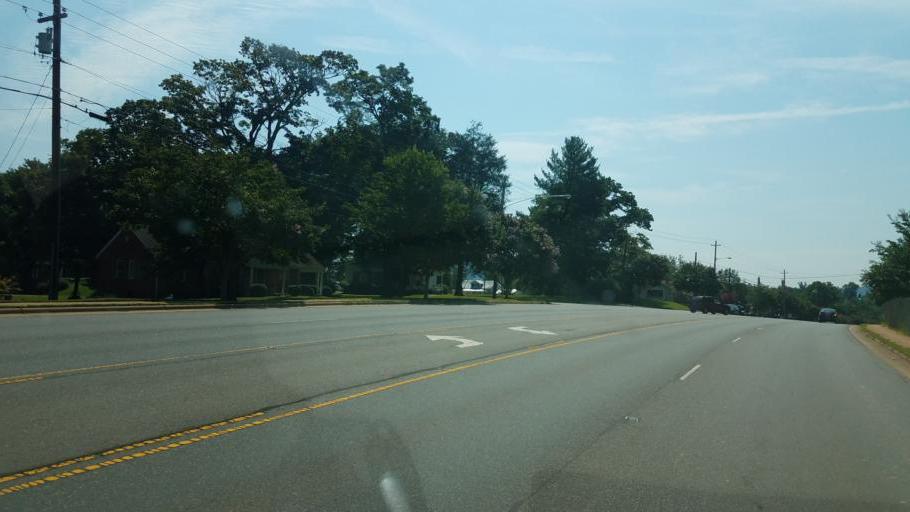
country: US
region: North Carolina
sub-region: Burke County
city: Morganton
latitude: 35.7346
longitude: -81.6745
